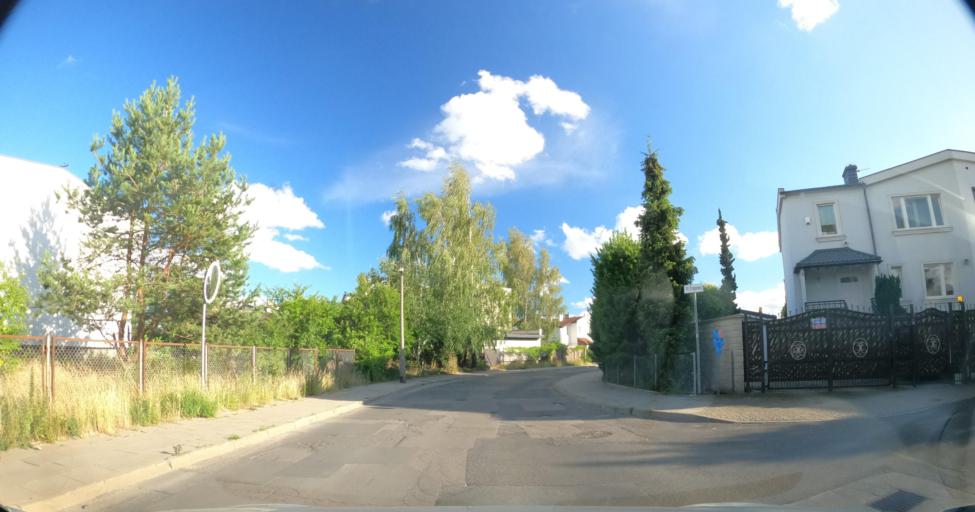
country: PL
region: Pomeranian Voivodeship
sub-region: Gdynia
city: Wielki Kack
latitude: 54.4289
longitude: 18.4742
